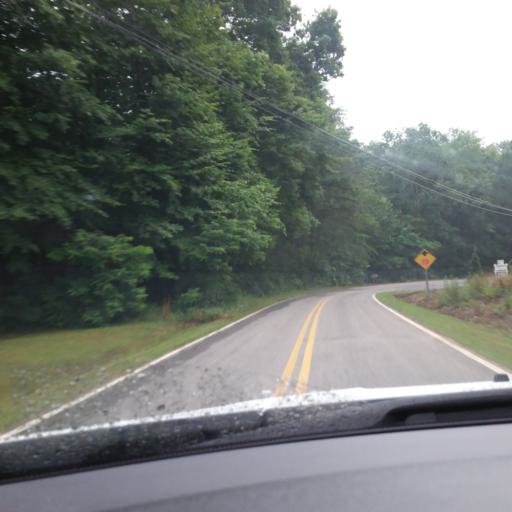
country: US
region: North Carolina
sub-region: Yancey County
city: Burnsville
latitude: 35.8310
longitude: -82.1981
